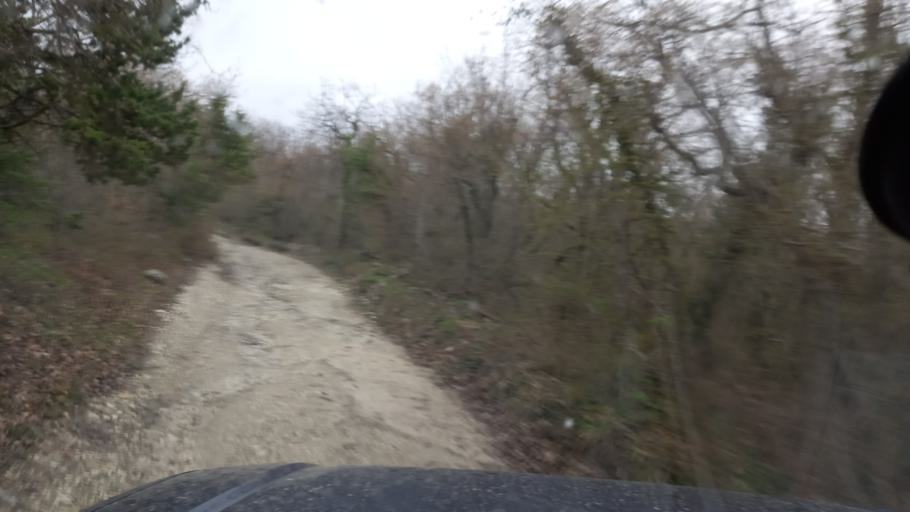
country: RU
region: Krasnodarskiy
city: Dzhubga
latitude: 44.3205
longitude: 38.6756
